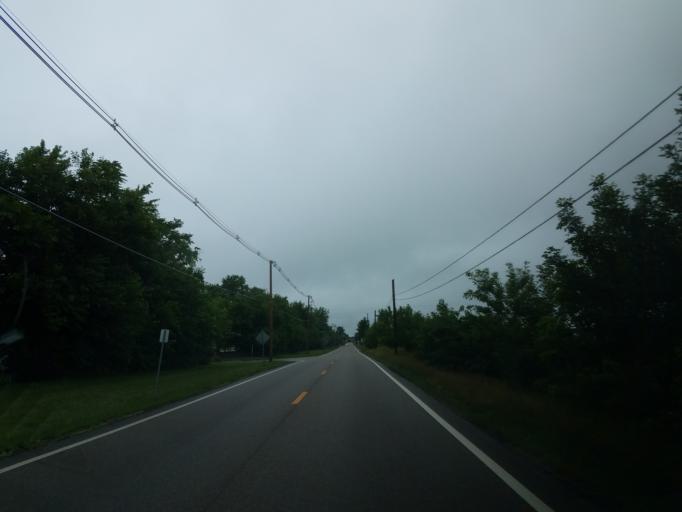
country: US
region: Illinois
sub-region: McLean County
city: Bloomington
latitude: 40.4524
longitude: -88.9813
